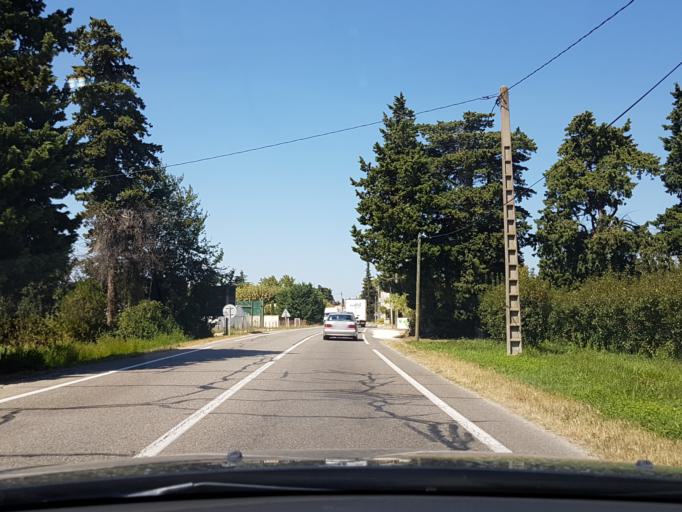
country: FR
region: Provence-Alpes-Cote d'Azur
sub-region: Departement des Bouches-du-Rhone
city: Chateaurenard
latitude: 43.8785
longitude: 4.8337
